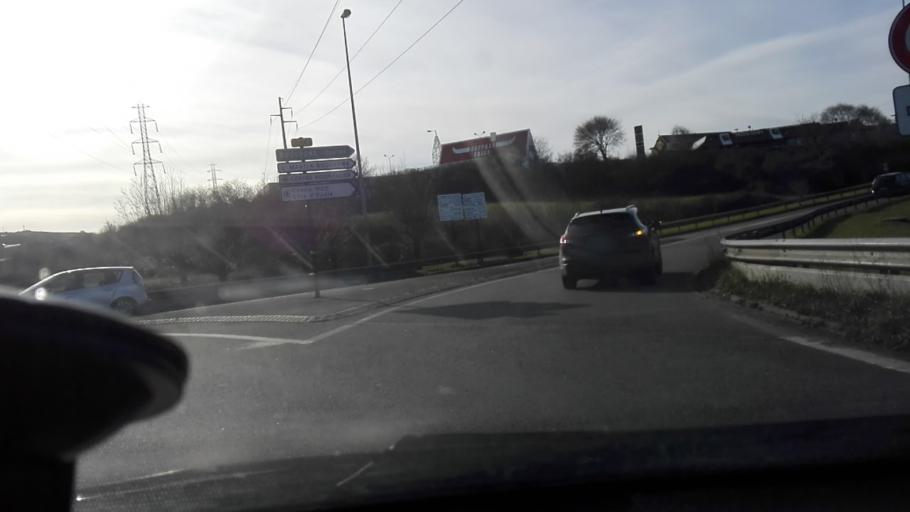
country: FR
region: Nord-Pas-de-Calais
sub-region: Departement du Pas-de-Calais
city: Saint-Martin-Boulogne
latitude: 50.7281
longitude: 1.6464
